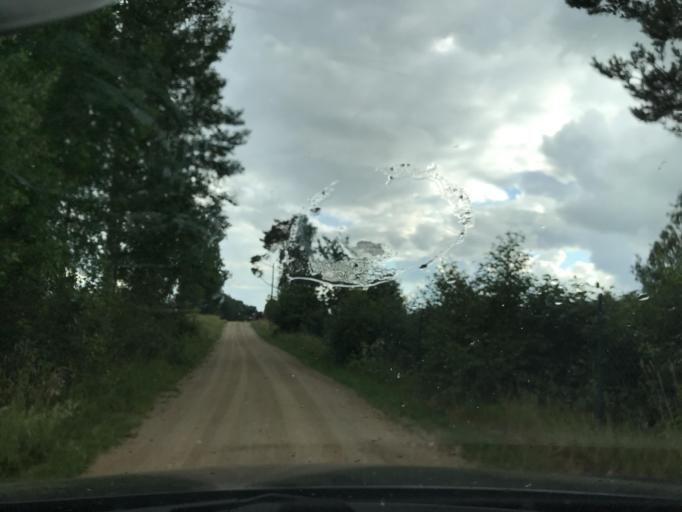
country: LV
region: Alsunga
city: Alsunga
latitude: 56.9811
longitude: 21.6336
